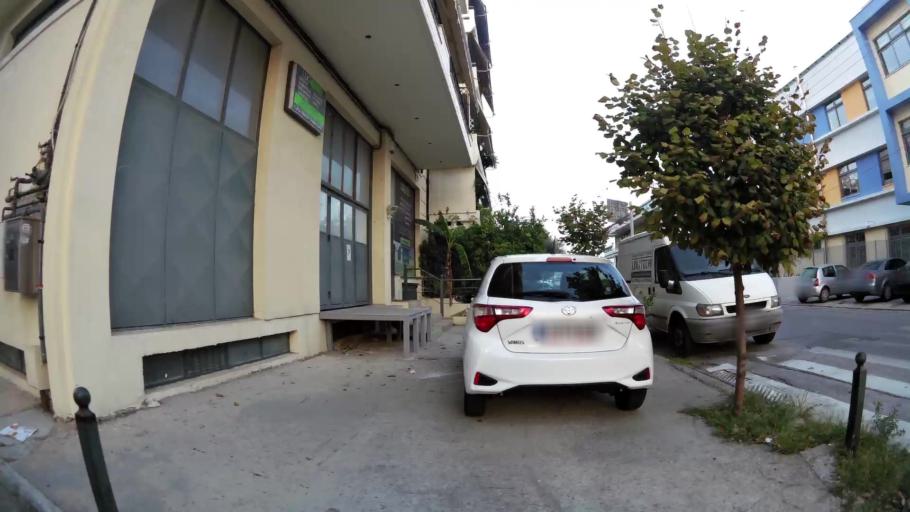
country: GR
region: Attica
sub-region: Nomarchia Athinas
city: Ilion
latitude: 38.0274
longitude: 23.6964
